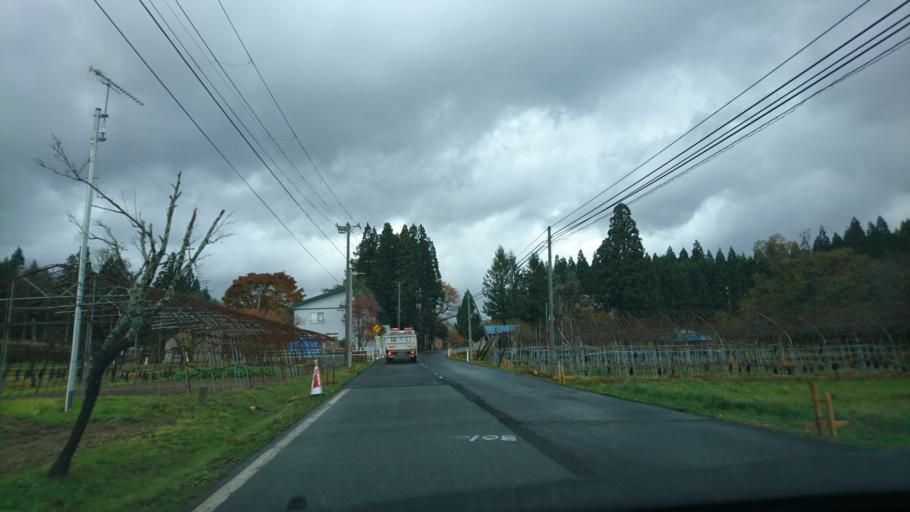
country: JP
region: Iwate
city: Shizukuishi
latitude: 39.5225
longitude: 140.8276
